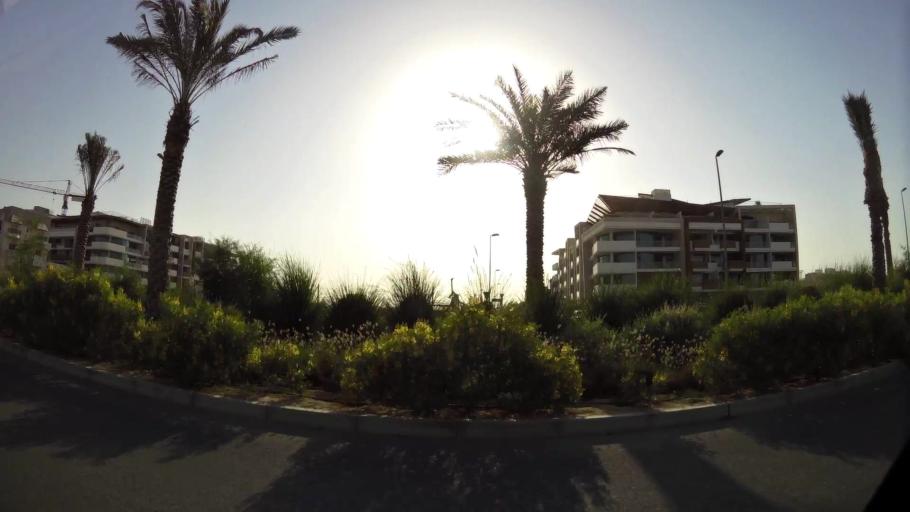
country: AE
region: Dubai
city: Dubai
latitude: 25.0577
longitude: 55.2004
